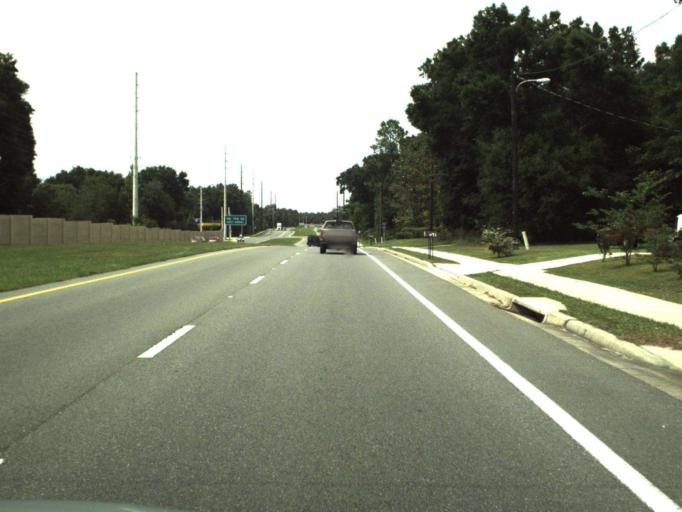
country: US
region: Florida
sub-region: Marion County
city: Ocala
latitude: 29.1908
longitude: -82.0535
